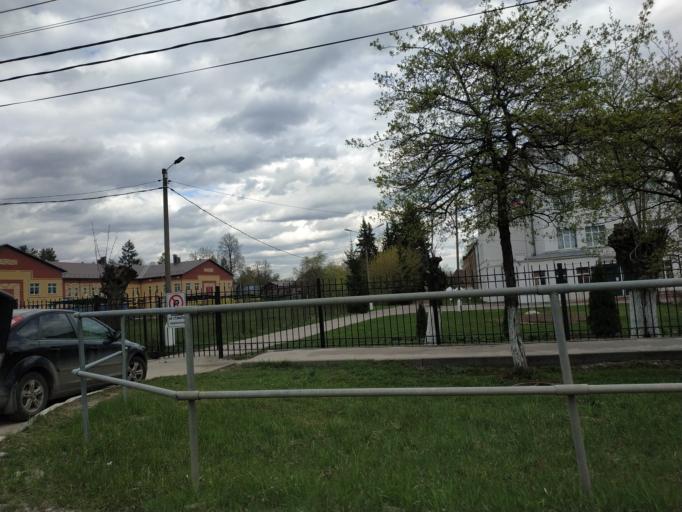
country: RU
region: Moskovskaya
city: Pavlovskiy Posad
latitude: 55.7853
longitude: 38.6485
